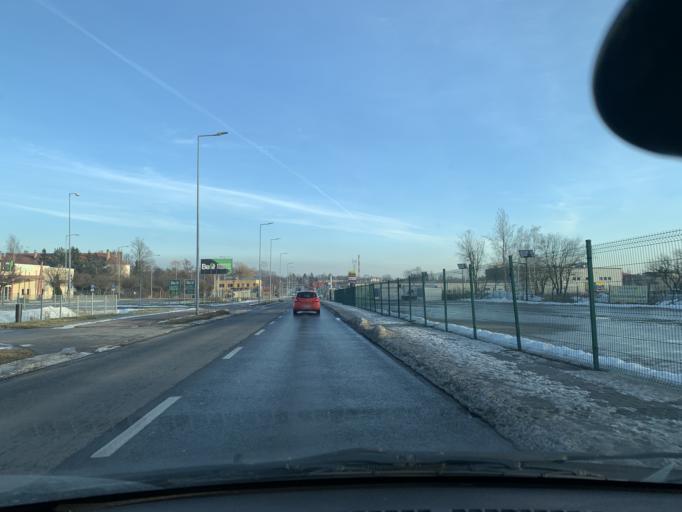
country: PL
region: Silesian Voivodeship
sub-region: Powiat tarnogorski
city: Radzionkow
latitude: 50.3982
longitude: 18.8935
